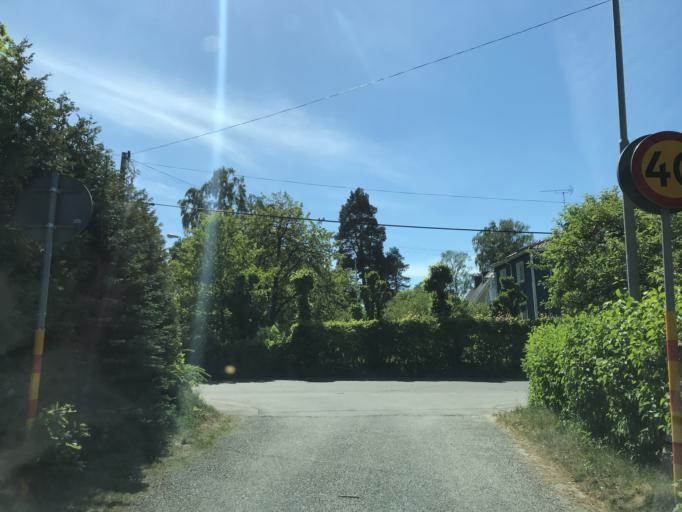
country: SE
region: Stockholm
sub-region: Sollentuna Kommun
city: Sollentuna
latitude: 59.4253
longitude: 17.9623
